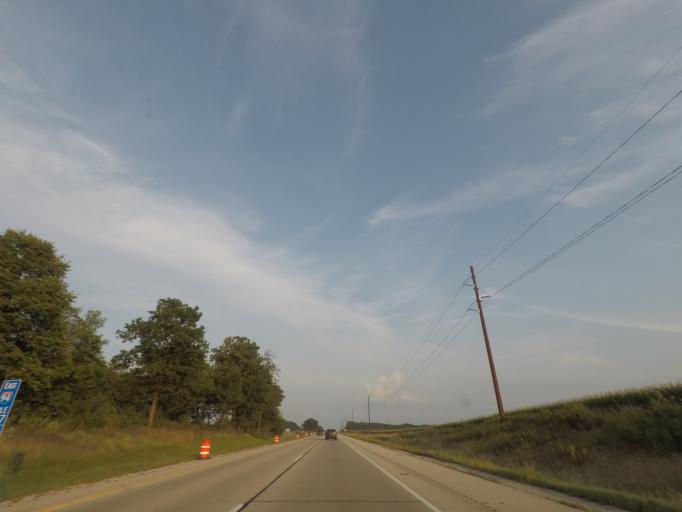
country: US
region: Wisconsin
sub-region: Jefferson County
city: Lake Mills
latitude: 43.1054
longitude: -88.9446
